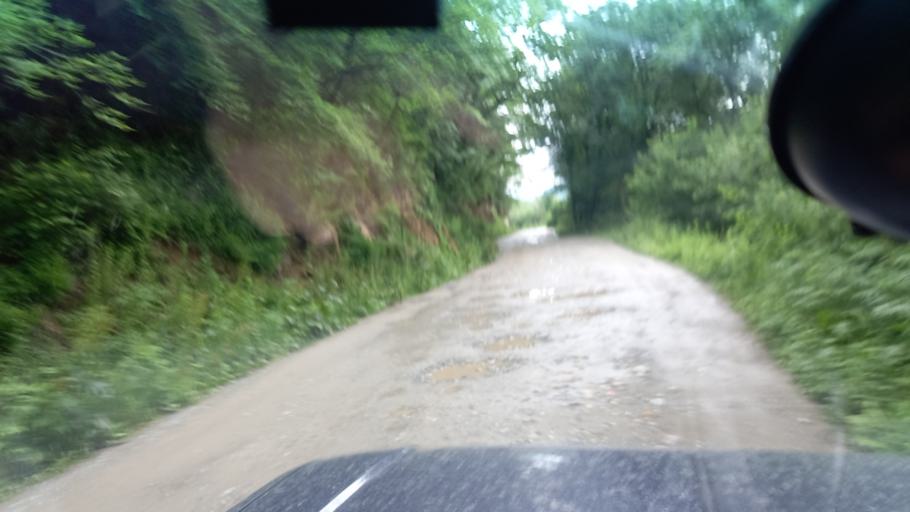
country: RU
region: Krasnodarskiy
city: Psebay
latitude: 44.0395
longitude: 40.7541
